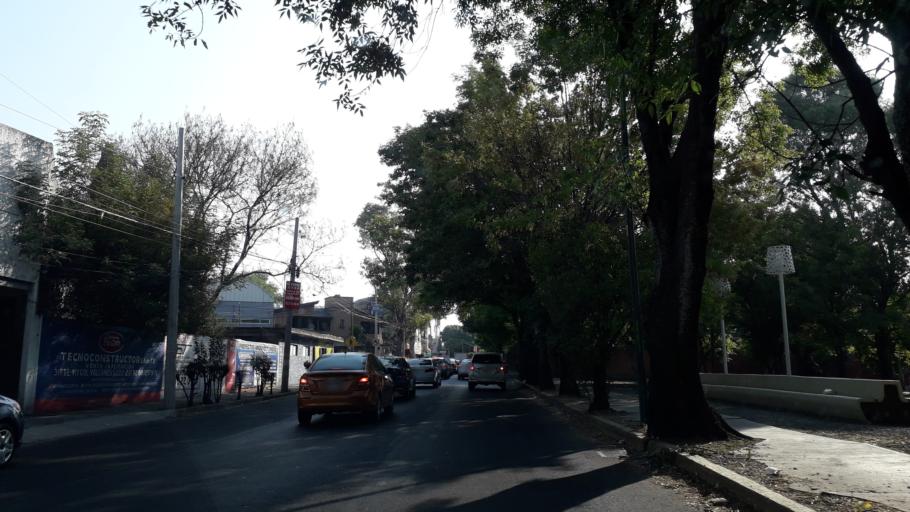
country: MX
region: Puebla
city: Puebla
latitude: 19.0385
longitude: -98.2240
